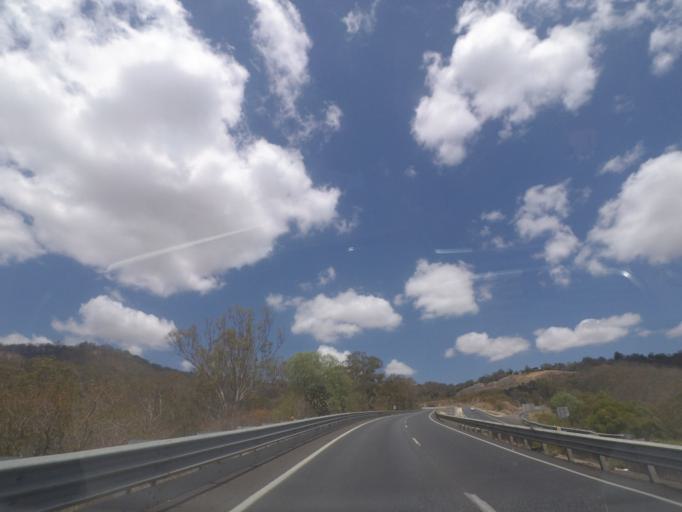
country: AU
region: Queensland
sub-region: Toowoomba
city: East Toowoomba
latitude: -27.5690
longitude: 151.9932
